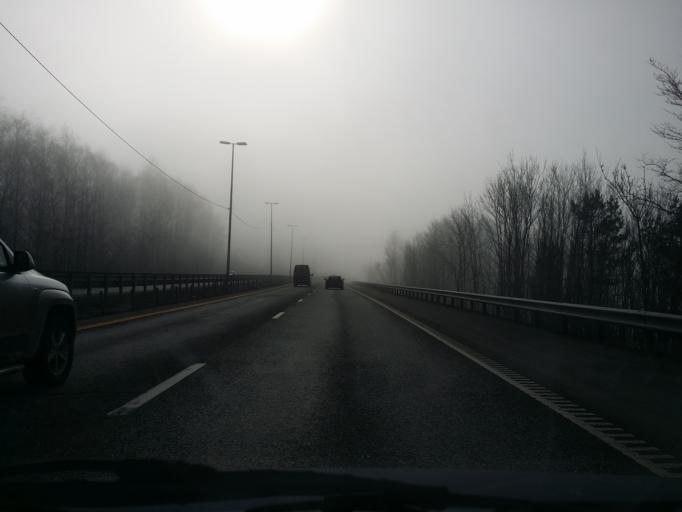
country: NO
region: Buskerud
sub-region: Lier
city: Tranby
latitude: 59.7818
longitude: 10.2745
